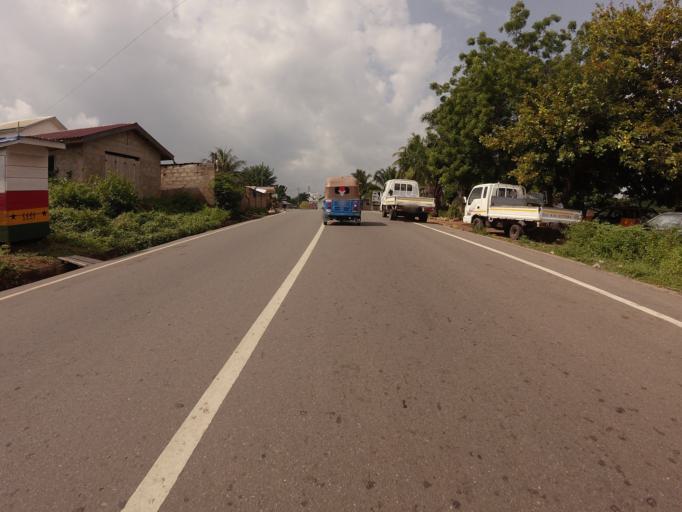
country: GH
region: Volta
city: Ho
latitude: 6.6221
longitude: 0.4800
